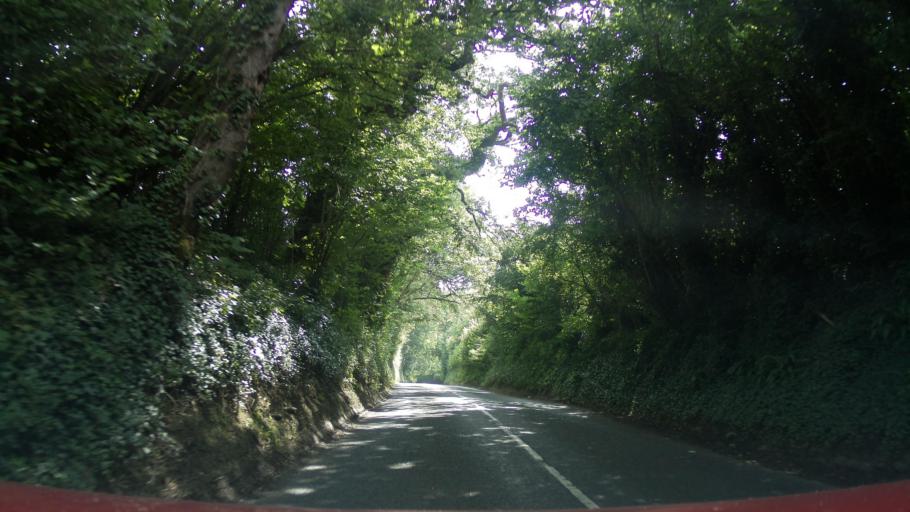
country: GB
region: England
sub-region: Somerset
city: Redlynch
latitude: 51.1065
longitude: -2.4381
